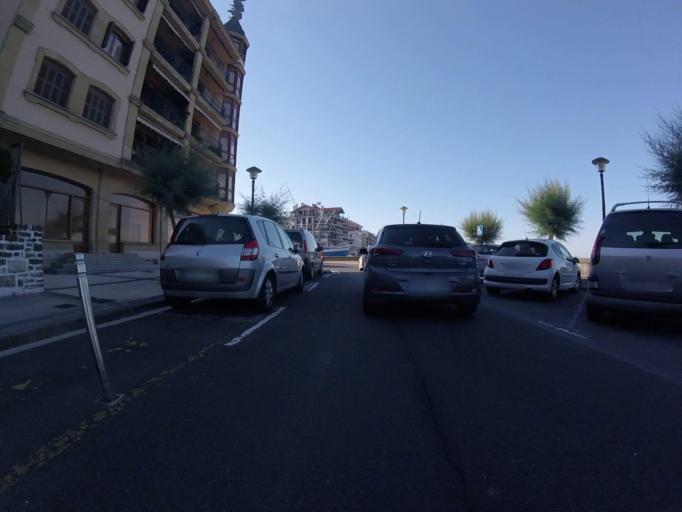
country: ES
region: Basque Country
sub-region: Provincia de Guipuzcoa
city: Fuenterrabia
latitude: 43.3671
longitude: -1.7918
